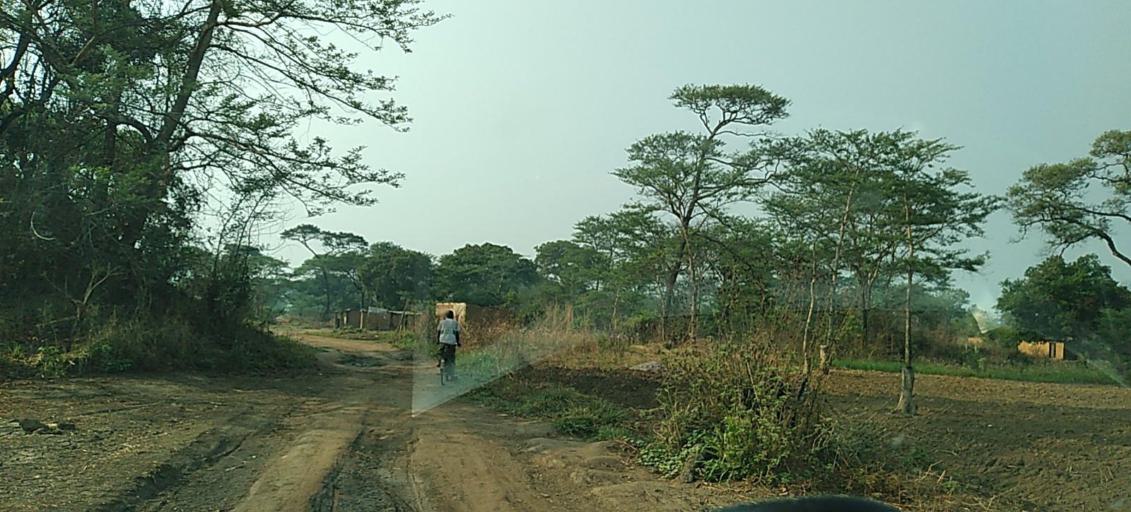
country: ZM
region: North-Western
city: Solwezi
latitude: -12.3695
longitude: 26.5584
